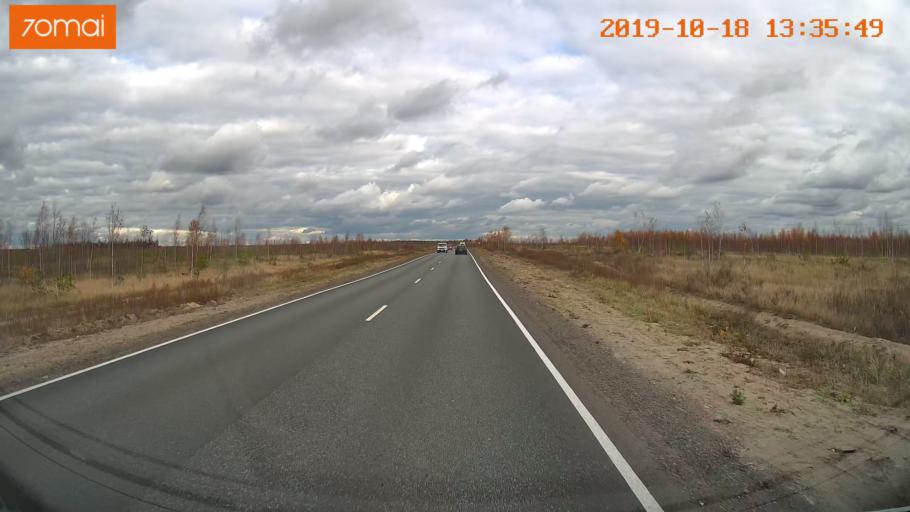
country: RU
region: Rjazan
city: Solotcha
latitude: 54.8638
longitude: 39.9761
